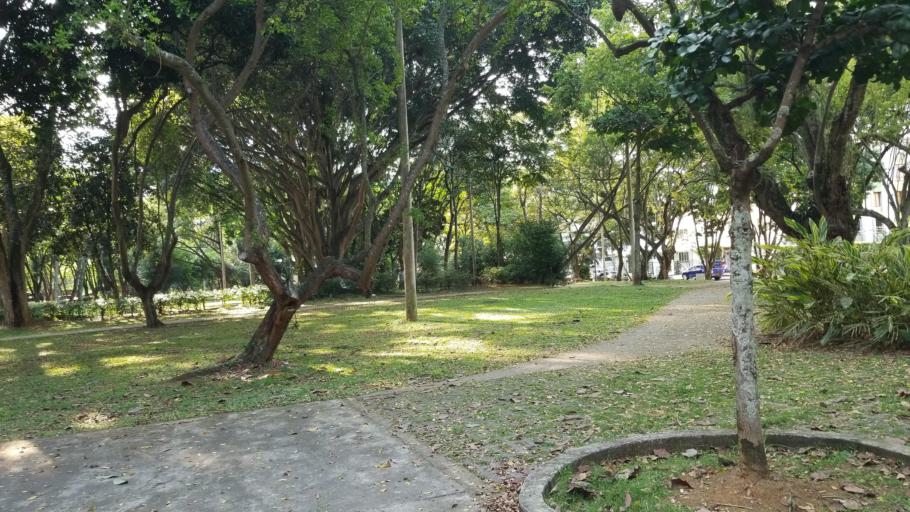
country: CO
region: Valle del Cauca
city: Cali
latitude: 3.3836
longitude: -76.5412
